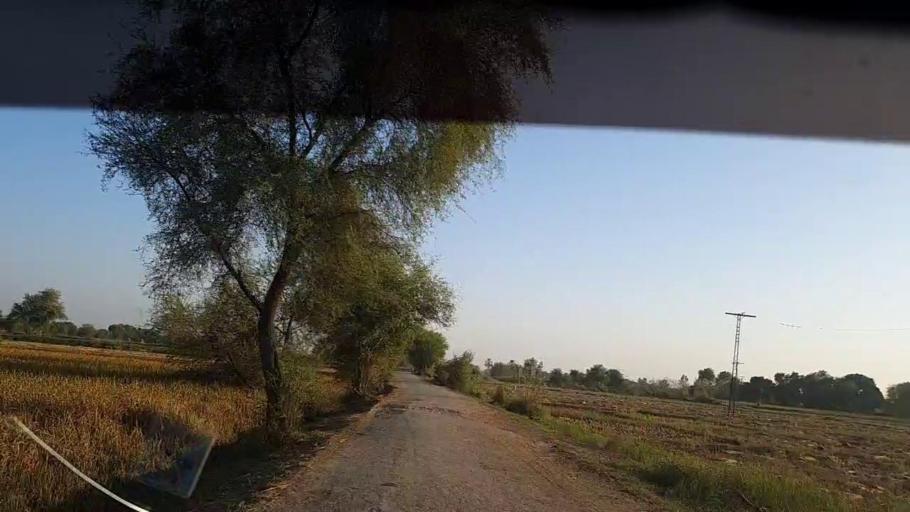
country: PK
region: Sindh
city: Ratodero
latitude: 27.8694
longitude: 68.1882
